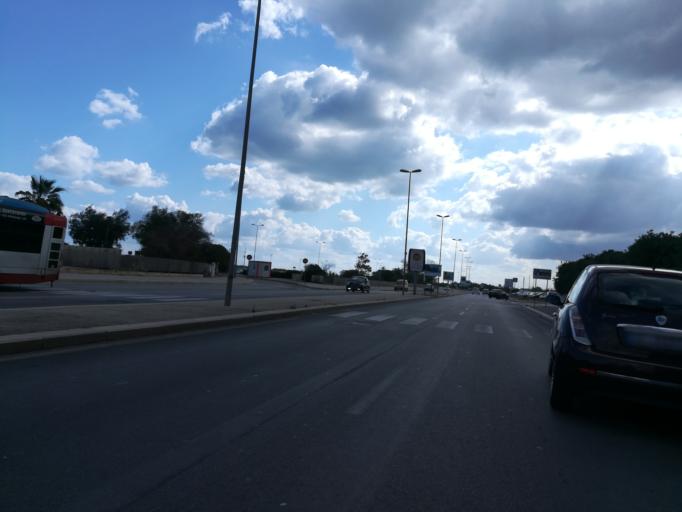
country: IT
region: Apulia
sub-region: Provincia di Bari
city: Bari
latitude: 41.1171
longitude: 16.8939
